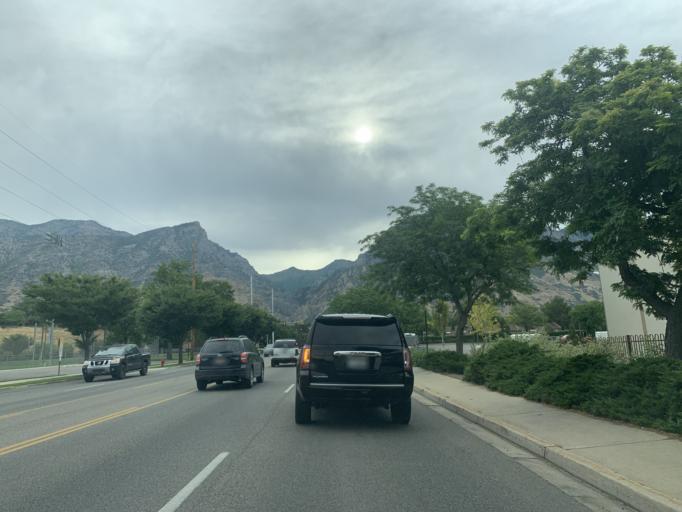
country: US
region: Utah
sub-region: Utah County
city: Provo
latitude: 40.2633
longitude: -111.6578
